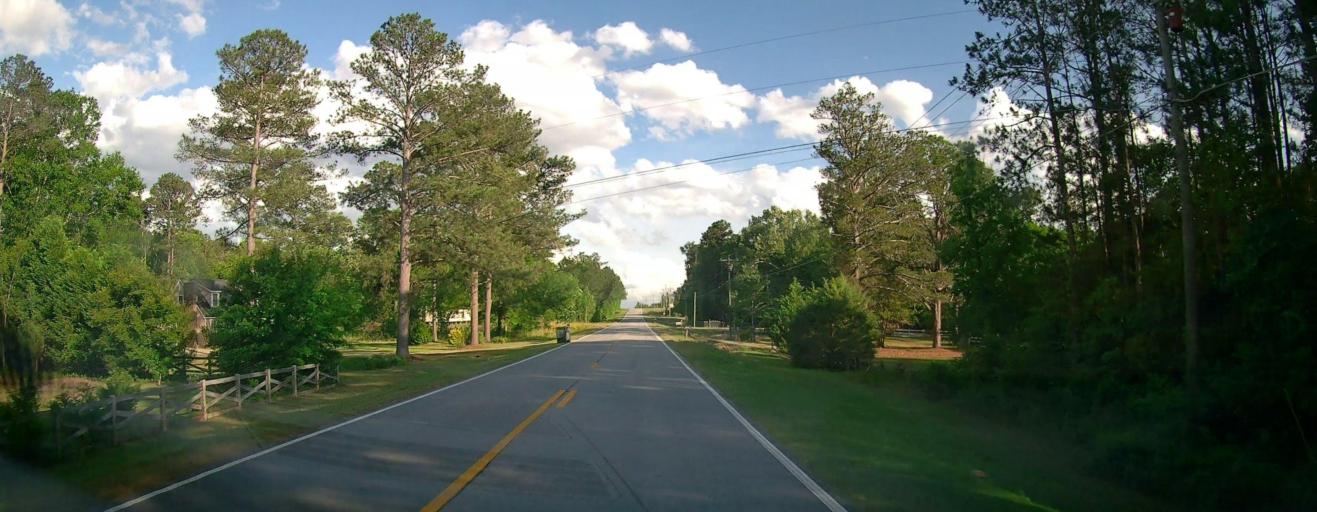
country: US
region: Georgia
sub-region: Peach County
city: Byron
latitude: 32.7006
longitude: -83.7785
